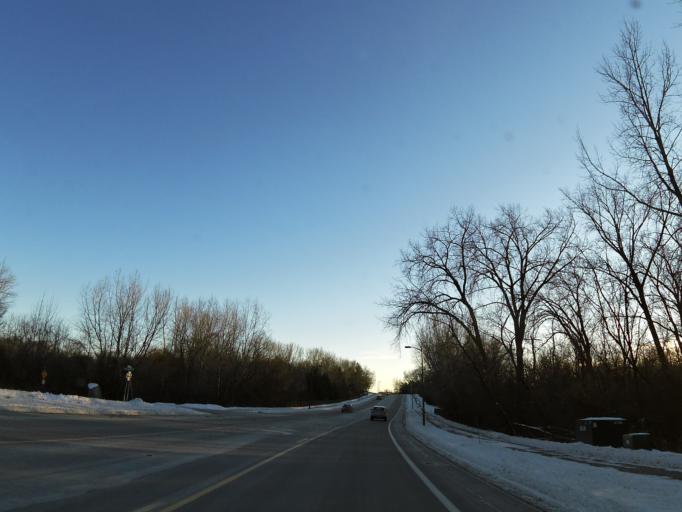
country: US
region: Minnesota
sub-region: Hennepin County
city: Shorewood
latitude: 44.8564
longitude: -93.5816
